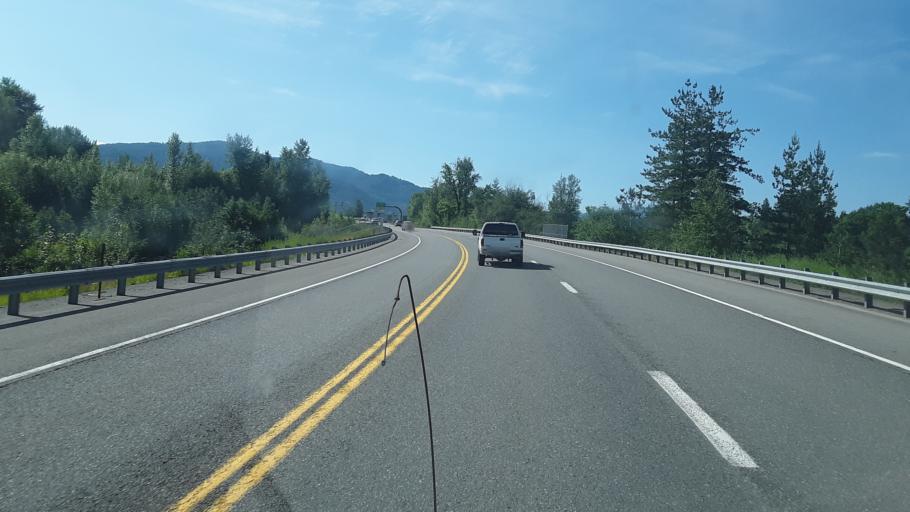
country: US
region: Idaho
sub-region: Bonner County
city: Sandpoint
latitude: 48.2844
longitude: -116.5501
